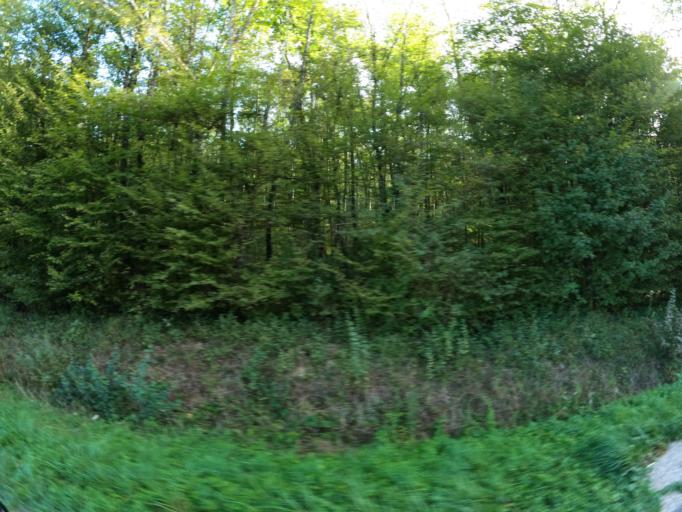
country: FR
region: Franche-Comte
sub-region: Departement du Jura
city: Montmorot
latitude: 46.7242
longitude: 5.5122
